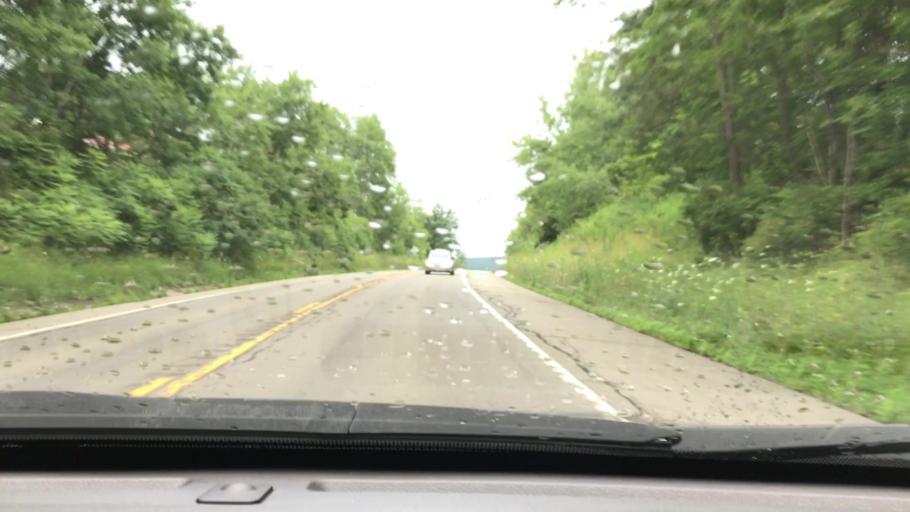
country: US
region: New York
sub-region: Cattaraugus County
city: Salamanca
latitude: 42.1882
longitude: -78.6772
